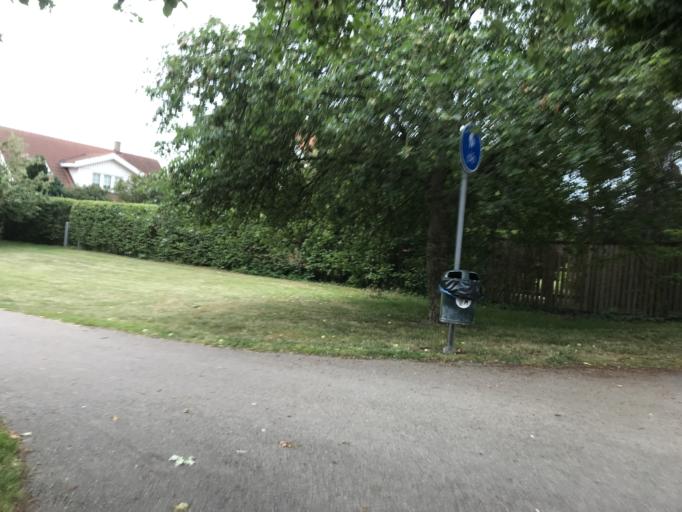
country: SE
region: Skane
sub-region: Landskrona
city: Landskrona
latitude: 55.8843
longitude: 12.8391
